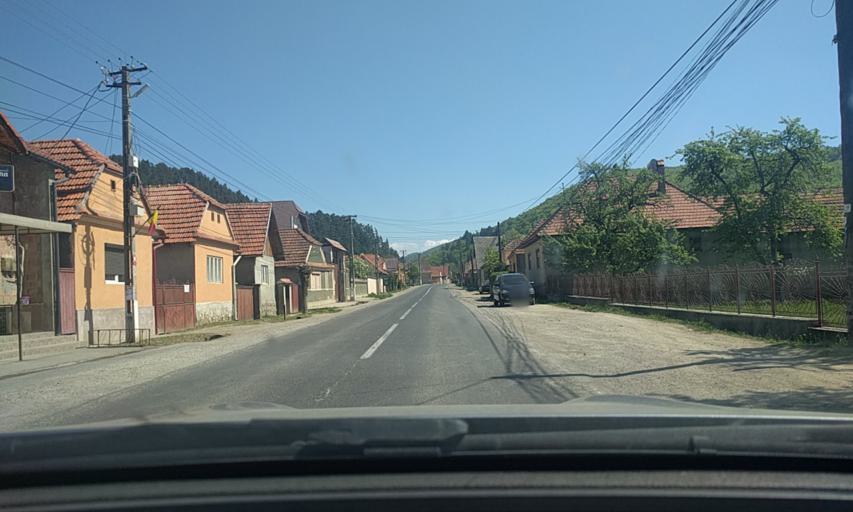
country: RO
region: Brasov
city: Tunelu-Teliu
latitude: 45.7005
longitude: 25.8522
